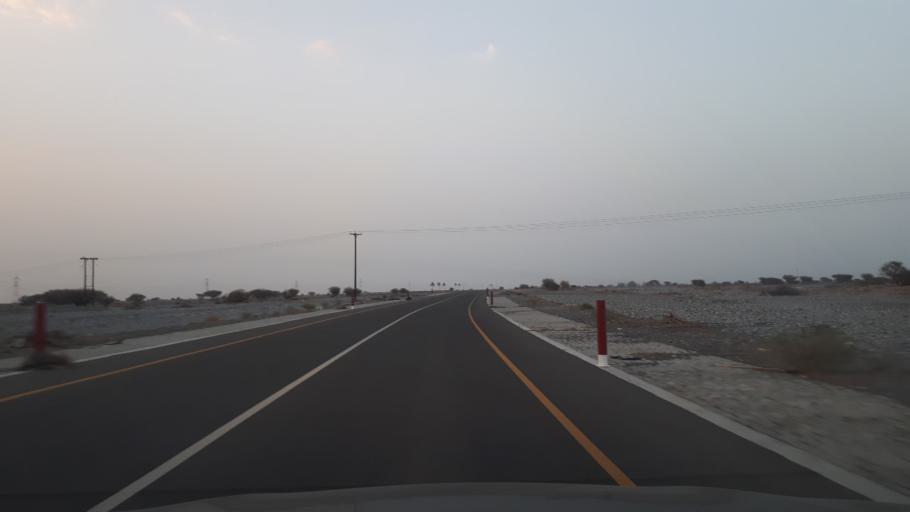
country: OM
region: Al Batinah
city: Rustaq
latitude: 23.5923
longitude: 57.5843
